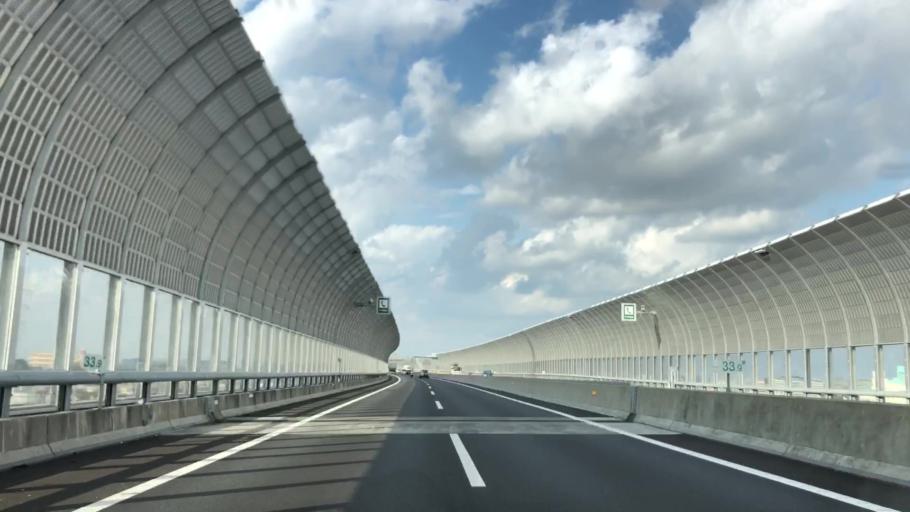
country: JP
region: Chiba
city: Matsudo
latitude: 35.8002
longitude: 139.8780
